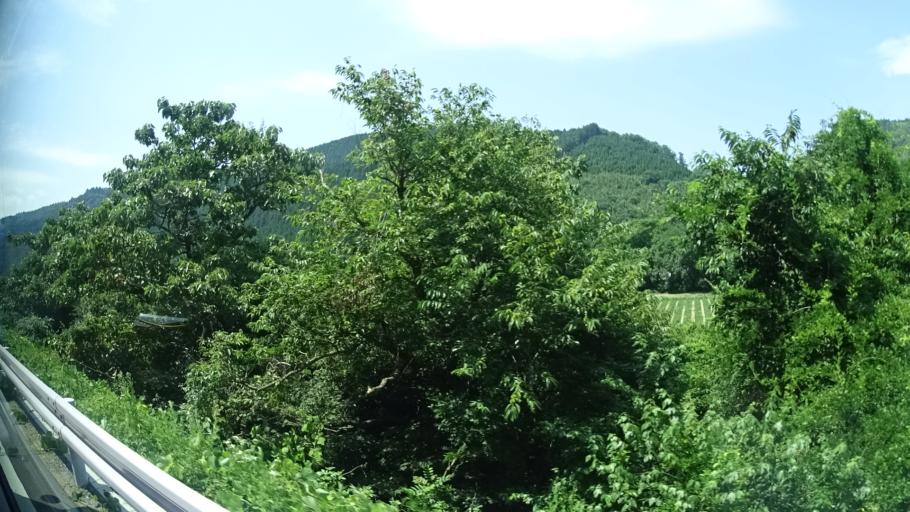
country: JP
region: Miyagi
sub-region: Oshika Gun
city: Onagawa Cho
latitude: 38.6328
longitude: 141.3619
